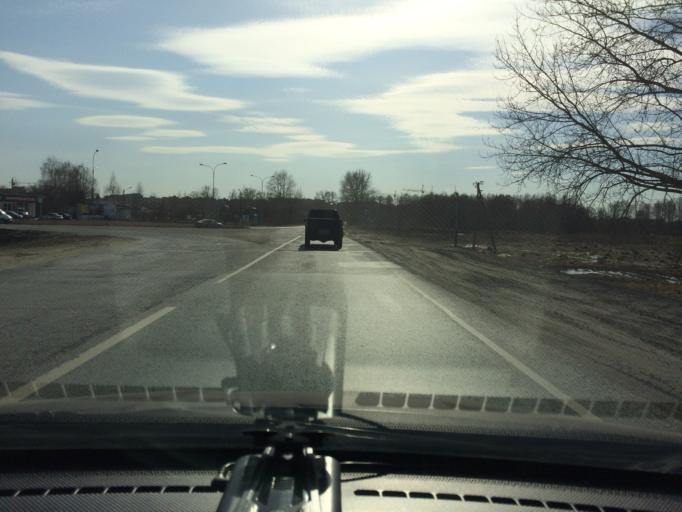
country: RU
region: Mariy-El
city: Yoshkar-Ola
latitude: 56.6468
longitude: 47.9380
